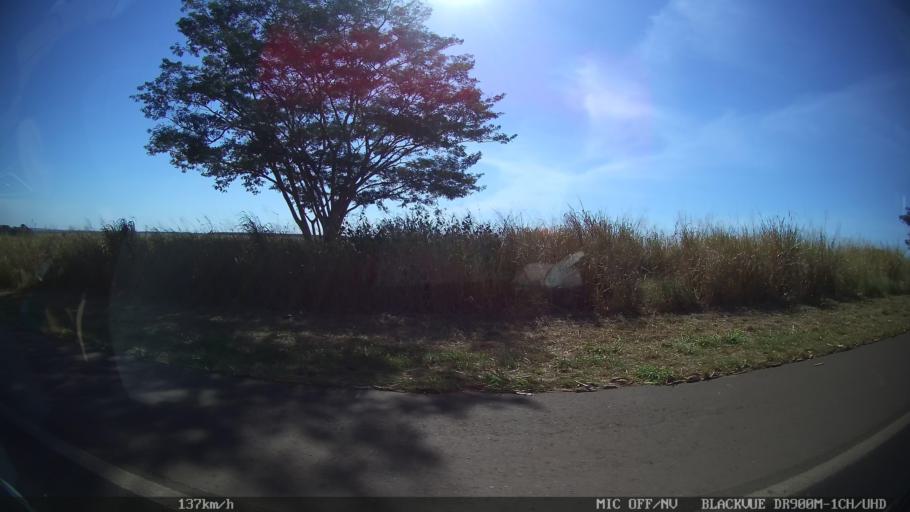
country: BR
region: Sao Paulo
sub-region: Olimpia
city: Olimpia
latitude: -20.6765
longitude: -48.8871
